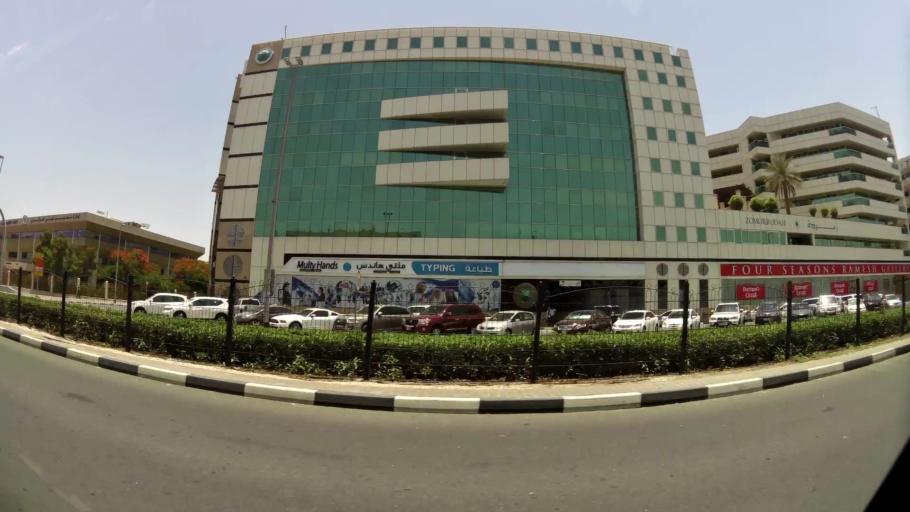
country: AE
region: Ash Shariqah
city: Sharjah
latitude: 25.2424
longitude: 55.3067
